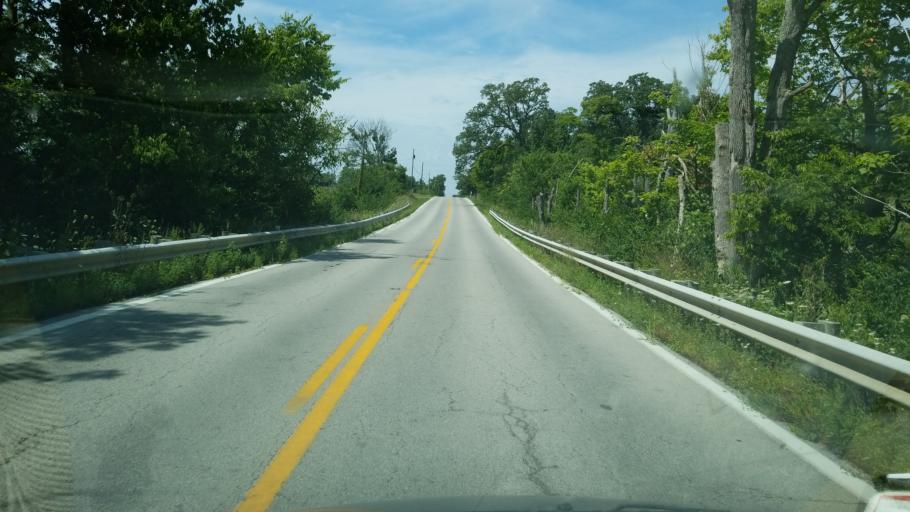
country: US
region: Ohio
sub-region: Madison County
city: West Jefferson
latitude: 39.8551
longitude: -83.2309
